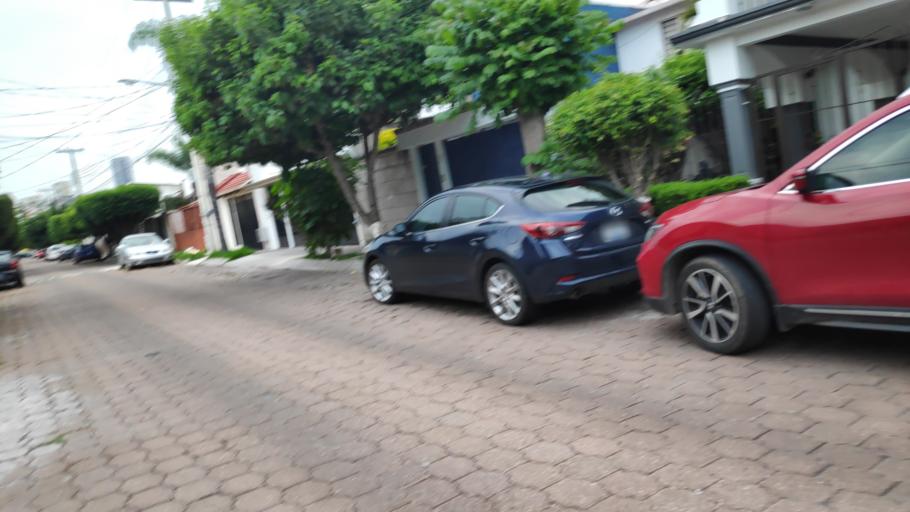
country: MX
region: Queretaro
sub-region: Queretaro
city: Santiago de Queretaro
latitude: 20.5843
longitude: -100.3671
